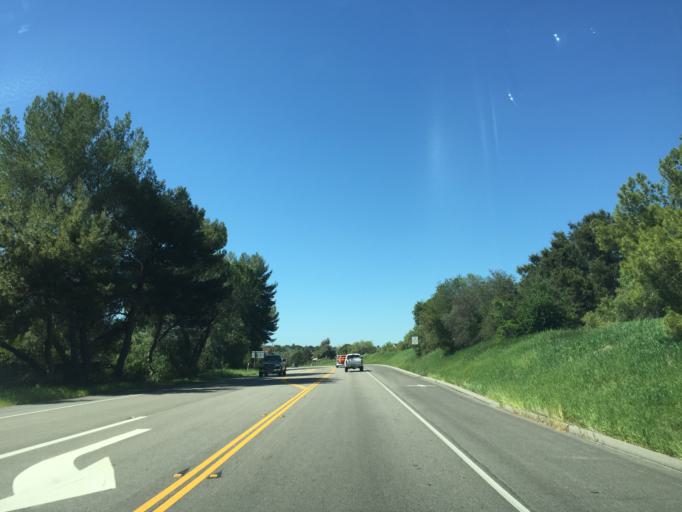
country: US
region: California
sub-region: Santa Barbara County
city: Los Olivos
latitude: 34.6663
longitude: -120.1112
